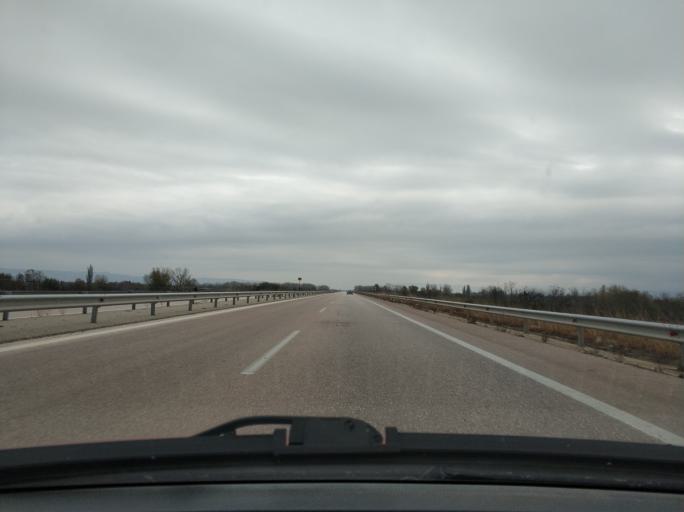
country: GR
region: Central Macedonia
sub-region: Nomos Thessalonikis
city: Kavallari
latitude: 40.7335
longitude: 23.0445
